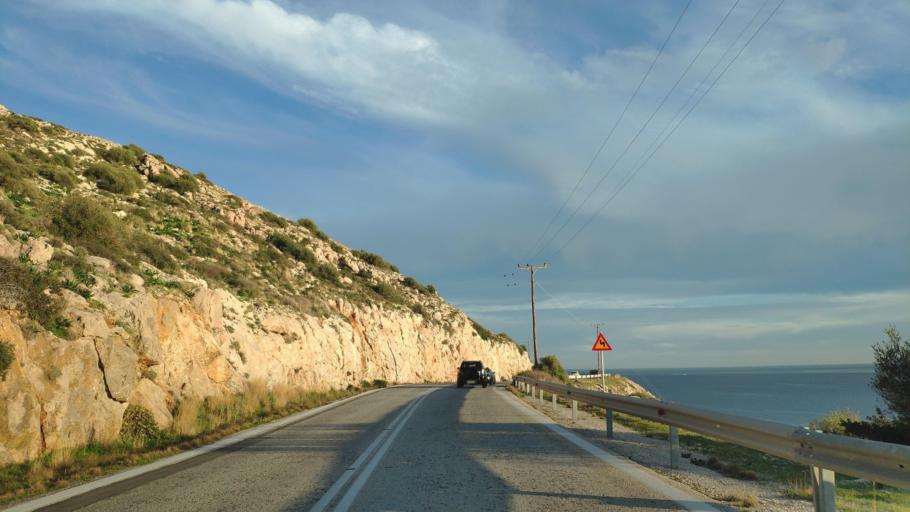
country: GR
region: Attica
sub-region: Nomarchia Anatolikis Attikis
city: Palaia Fokaia
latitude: 37.6706
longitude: 23.9495
